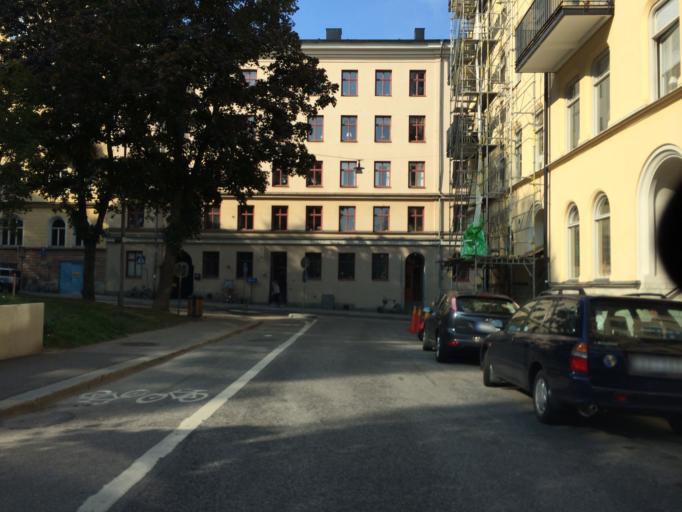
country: SE
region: Stockholm
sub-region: Stockholms Kommun
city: Stockholm
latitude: 59.3335
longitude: 18.0348
